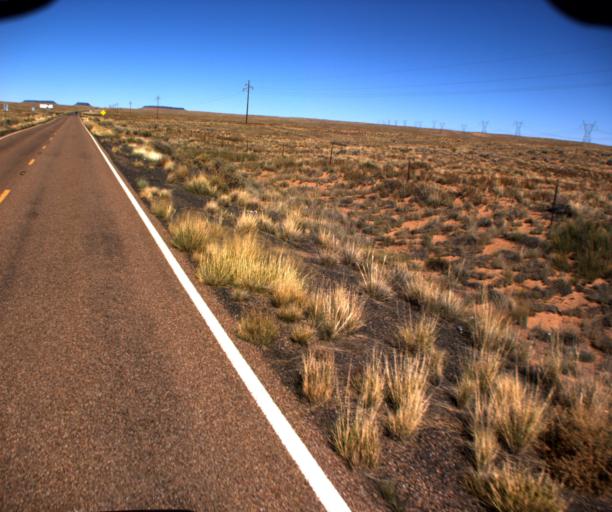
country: US
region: Arizona
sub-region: Navajo County
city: Holbrook
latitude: 35.1678
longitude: -110.0789
